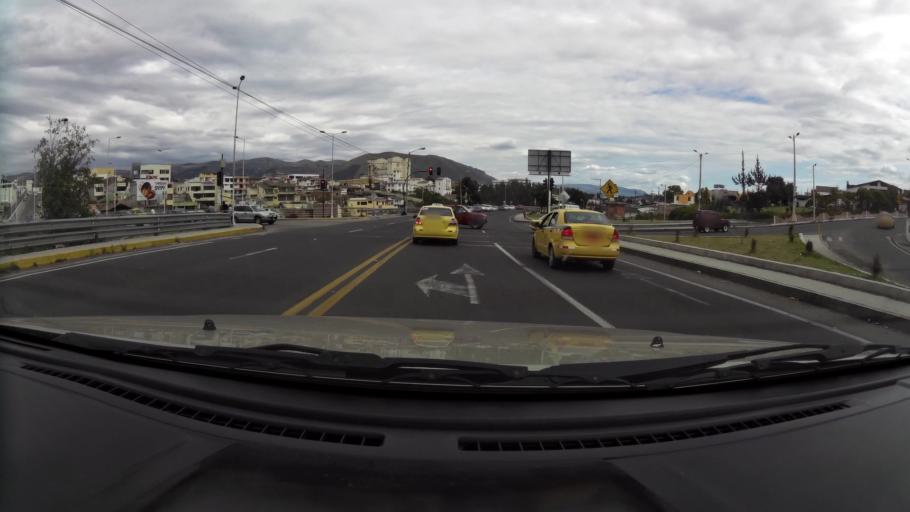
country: EC
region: Cotopaxi
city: Latacunga
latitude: -0.9484
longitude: -78.6154
